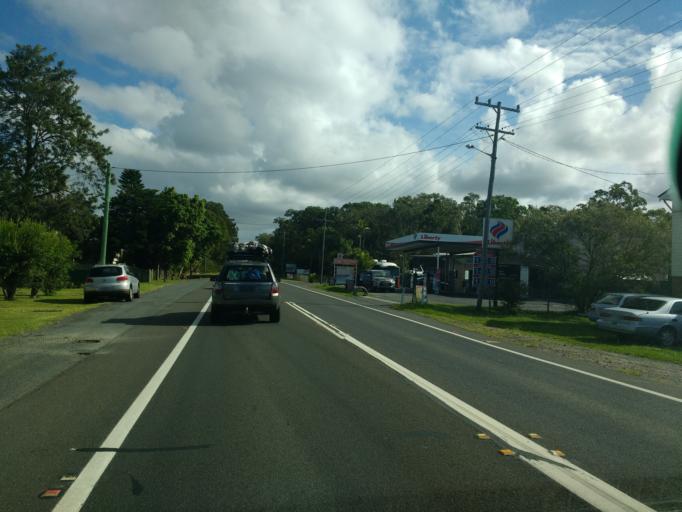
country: AU
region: New South Wales
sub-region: Richmond Valley
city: Evans Head
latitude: -29.0199
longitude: 153.4246
